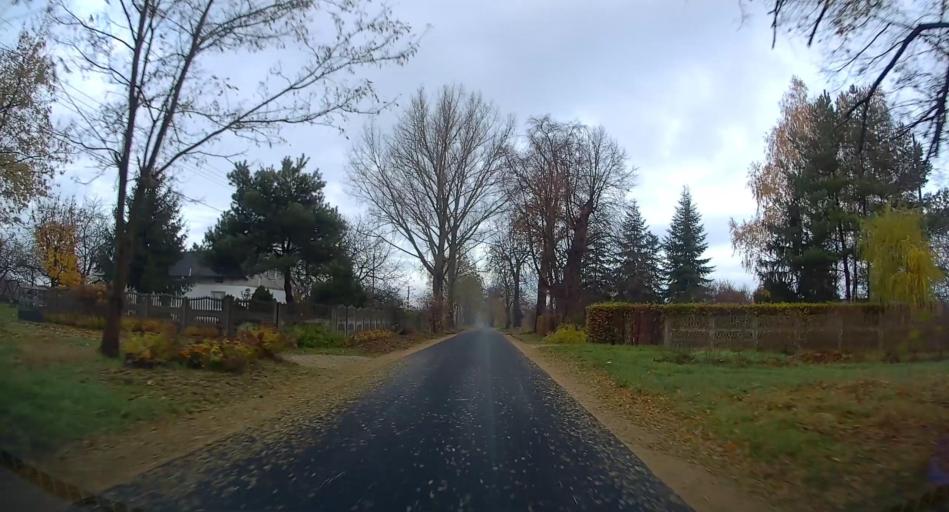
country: PL
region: Lodz Voivodeship
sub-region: Powiat skierniewicki
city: Kowiesy
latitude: 51.9240
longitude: 20.4093
